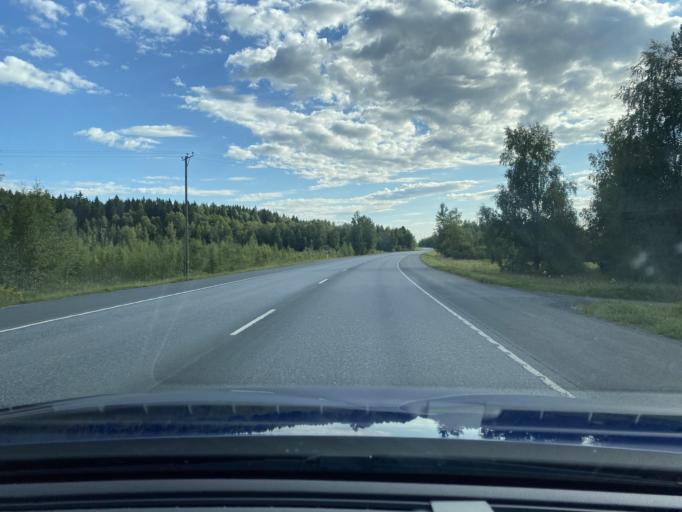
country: FI
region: Pirkanmaa
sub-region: Tampere
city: Lempaeaelae
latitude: 61.3389
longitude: 23.7859
